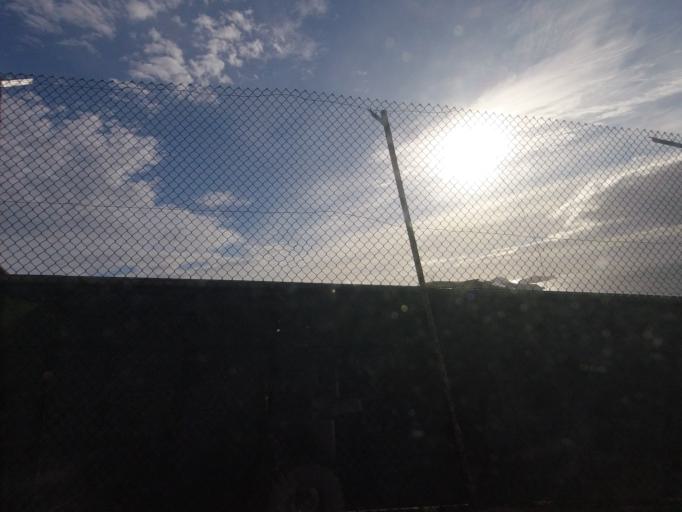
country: PT
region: Madeira
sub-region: Machico
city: Canical
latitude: 32.7462
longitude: -16.7391
